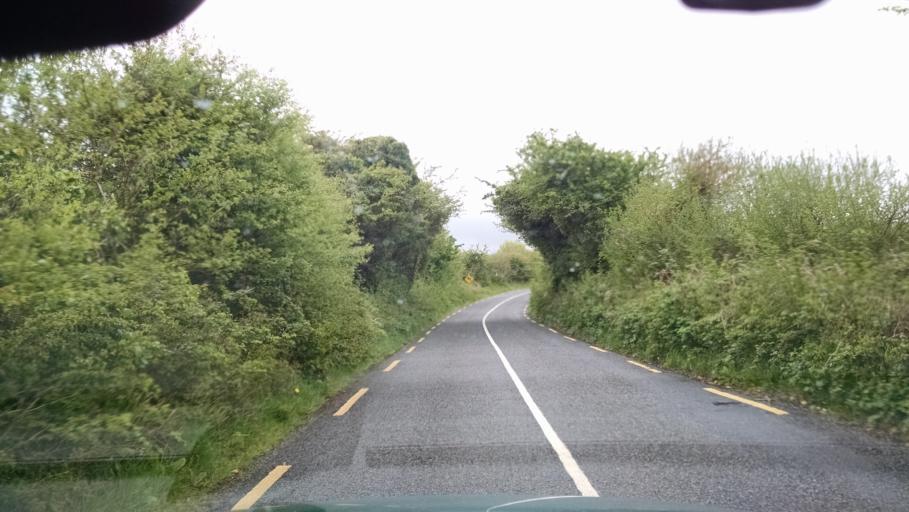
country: IE
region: Connaught
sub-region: County Galway
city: Bearna
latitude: 53.0865
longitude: -9.1620
